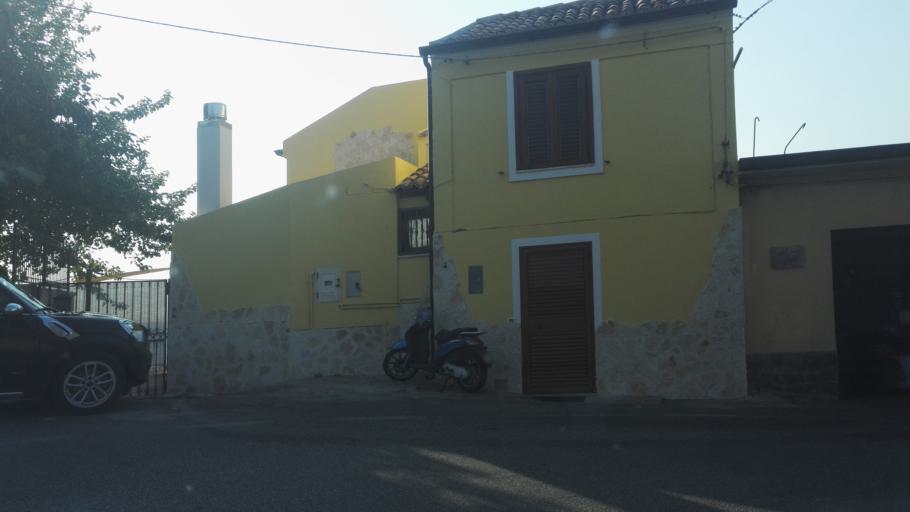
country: IT
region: Calabria
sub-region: Provincia di Vibo-Valentia
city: Maierato
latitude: 38.7337
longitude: 16.1613
